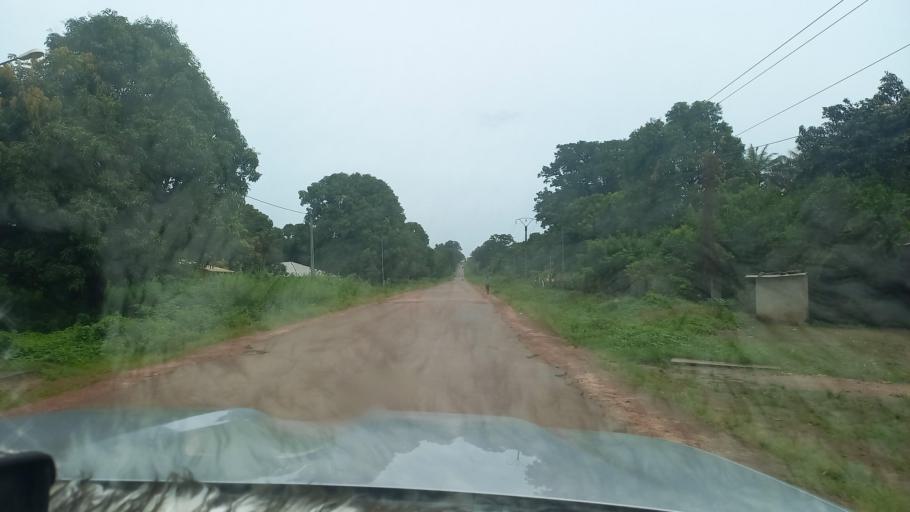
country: SN
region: Ziguinchor
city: Bignona
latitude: 12.8217
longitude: -16.1777
